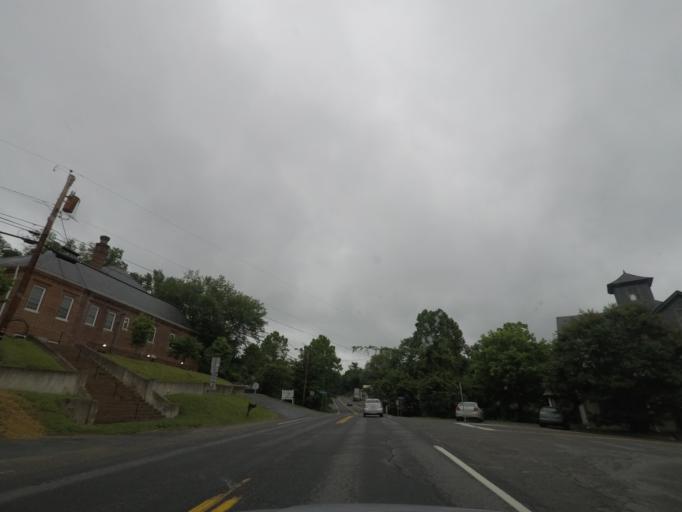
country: US
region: Virginia
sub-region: Fluvanna County
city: Palmyra
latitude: 37.8609
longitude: -78.2637
